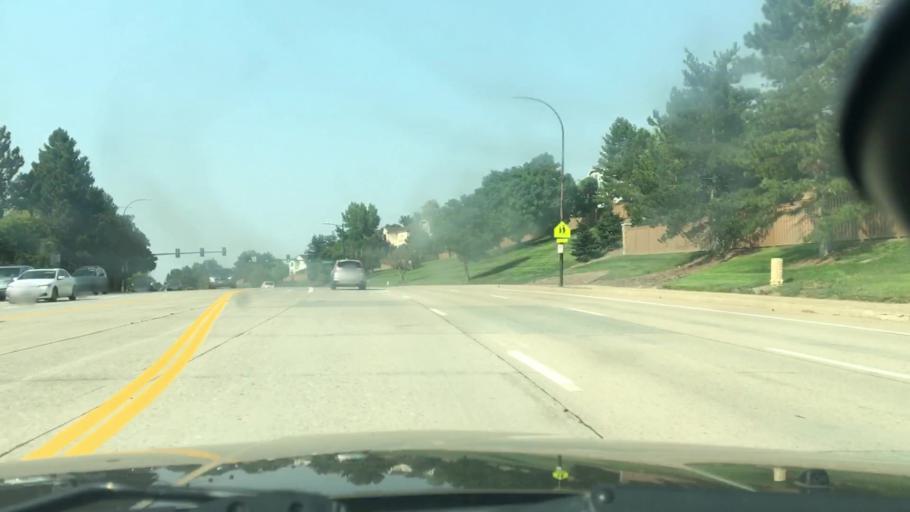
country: US
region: Colorado
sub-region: Douglas County
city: Carriage Club
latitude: 39.5454
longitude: -104.9103
